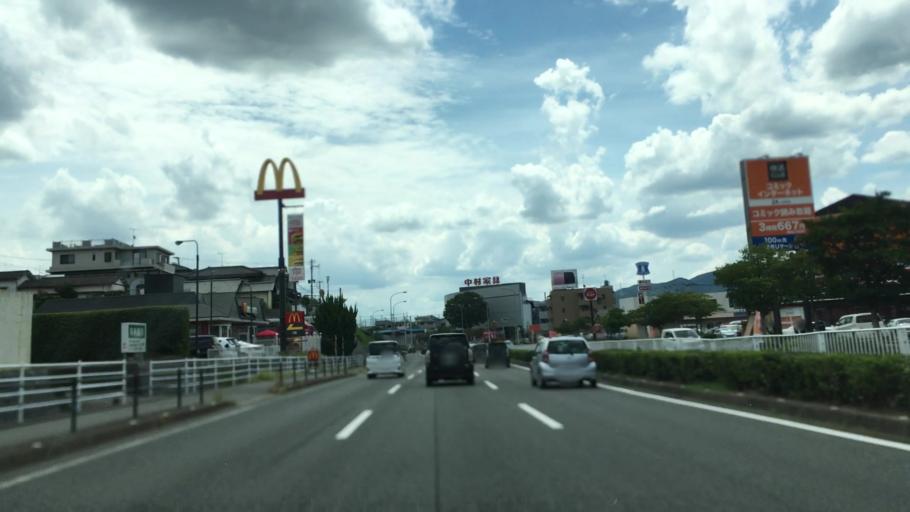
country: JP
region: Fukuoka
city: Dazaifu
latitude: 33.5018
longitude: 130.5314
